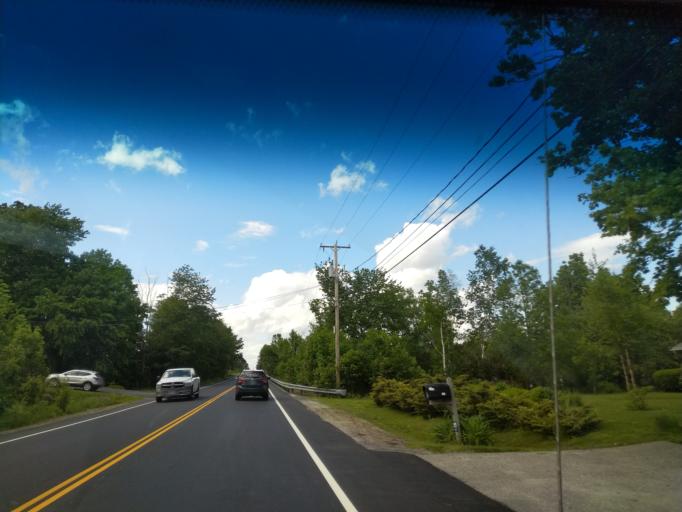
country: US
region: Maine
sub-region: Cumberland County
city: South Windham
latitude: 43.7200
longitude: -70.4186
